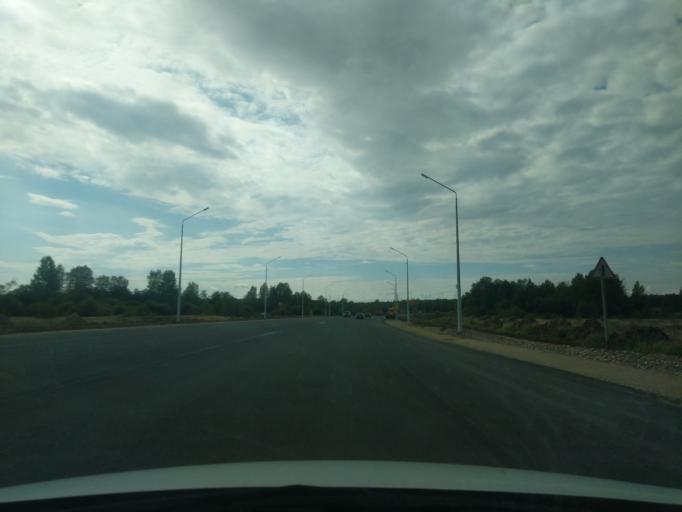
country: RU
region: Kostroma
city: Sudislavl'
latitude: 57.8286
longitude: 41.5366
